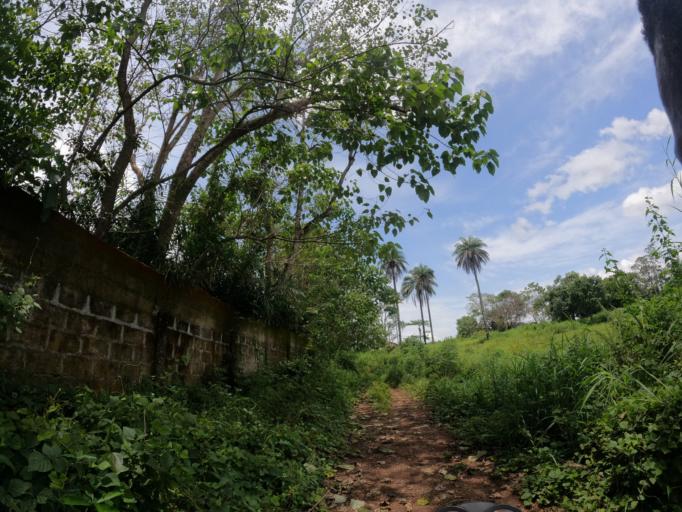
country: SL
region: Northern Province
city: Makeni
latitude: 9.1055
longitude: -12.2057
